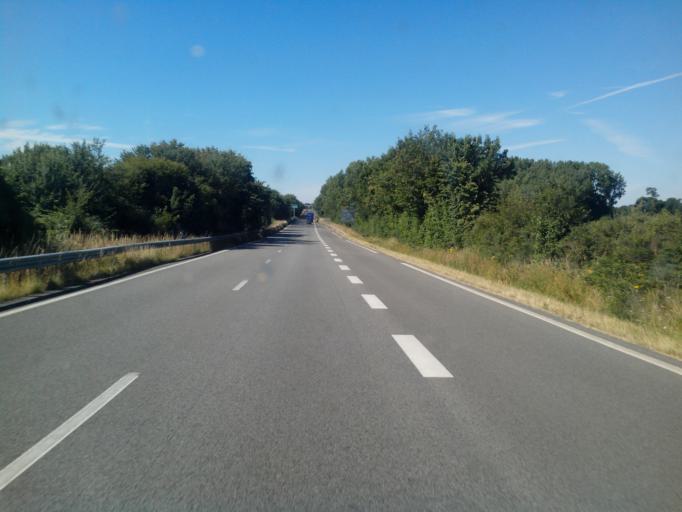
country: FR
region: Brittany
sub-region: Departement d'Ille-et-Vilaine
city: Grand-Fougeray
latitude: 47.6977
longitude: -1.7033
